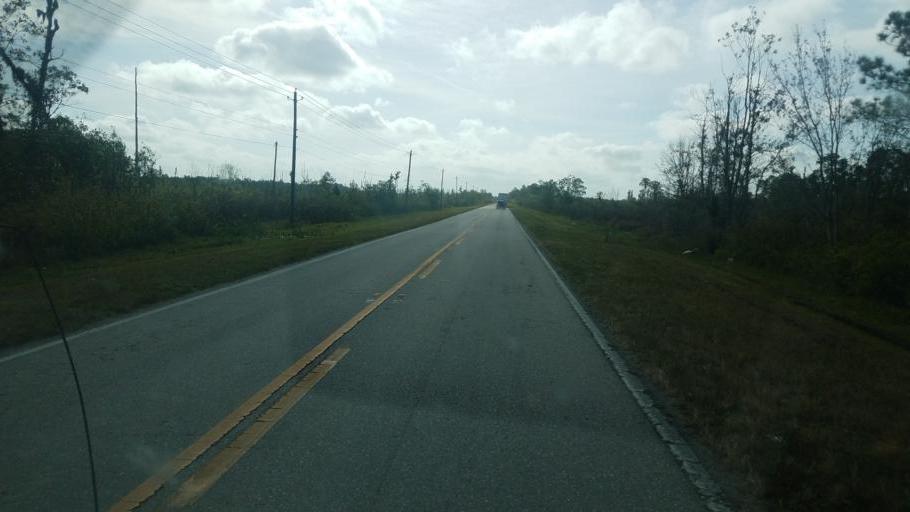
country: US
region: Florida
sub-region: Polk County
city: Polk City
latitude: 28.2051
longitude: -81.7558
